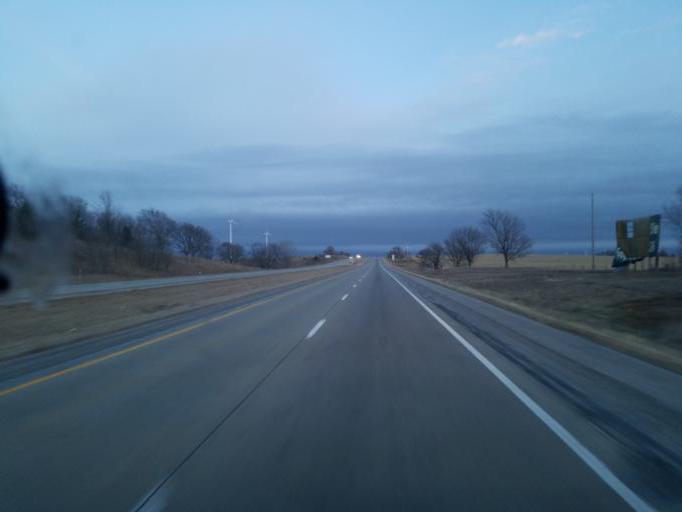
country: US
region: Iowa
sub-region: Pottawattamie County
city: Avoca
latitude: 41.4972
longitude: -95.2134
